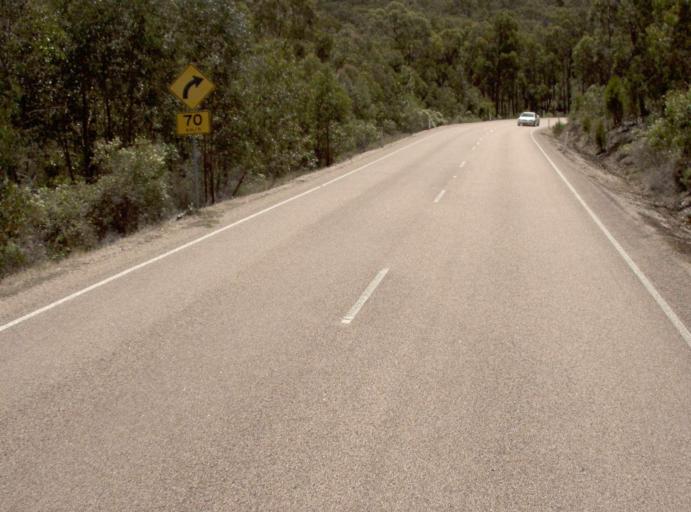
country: AU
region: Victoria
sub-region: East Gippsland
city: Lakes Entrance
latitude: -37.6100
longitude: 147.8809
